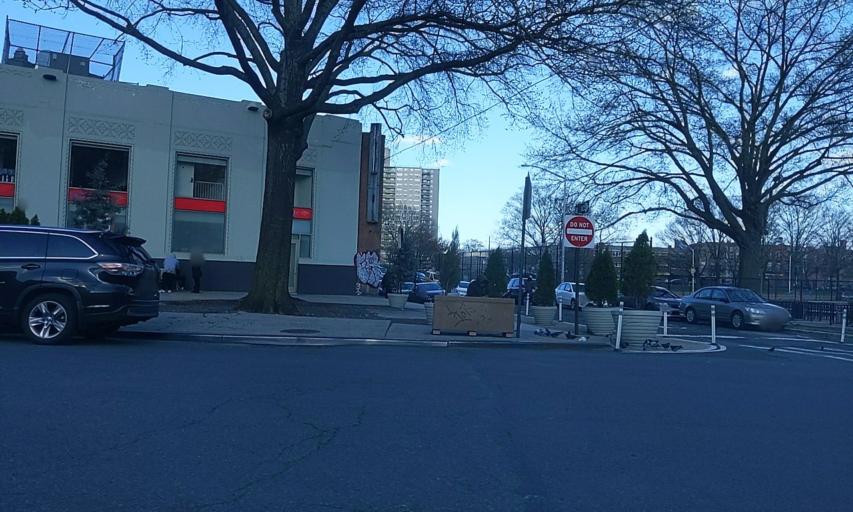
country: US
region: New York
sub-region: Bronx
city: The Bronx
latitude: 40.8292
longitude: -73.8744
